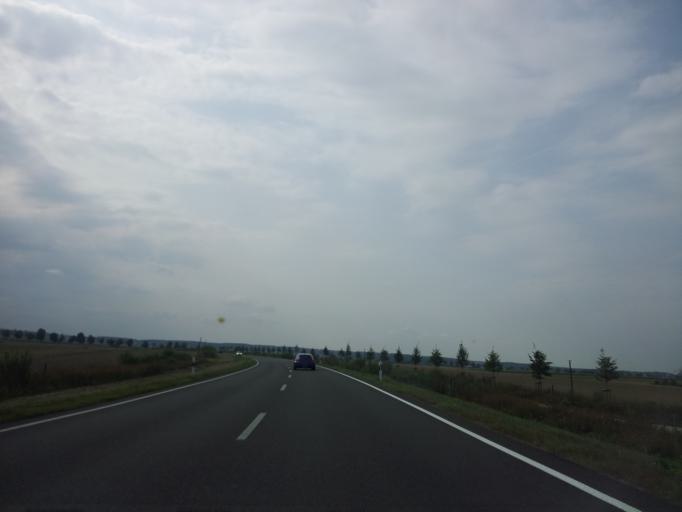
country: DE
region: Brandenburg
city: Niemegk
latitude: 52.1079
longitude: 12.6686
